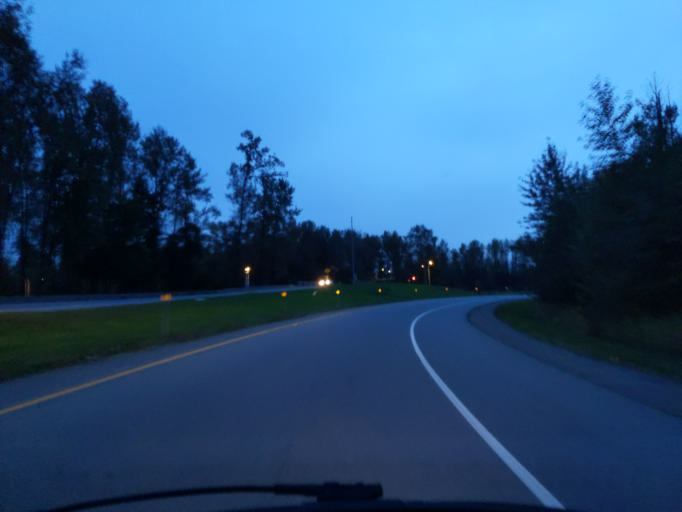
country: CA
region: British Columbia
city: Pitt Meadows
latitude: 49.1716
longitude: -122.6910
